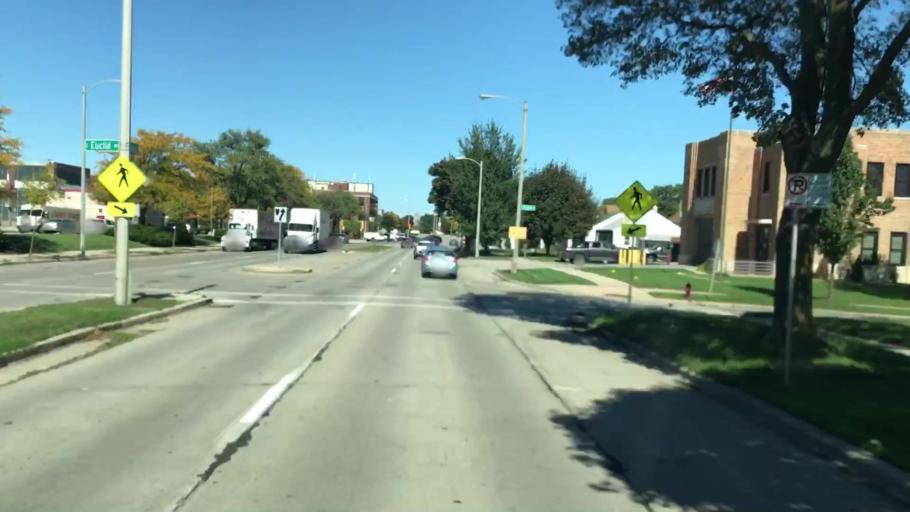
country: US
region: Wisconsin
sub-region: Milwaukee County
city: Saint Francis
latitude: 42.9863
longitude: -87.9094
